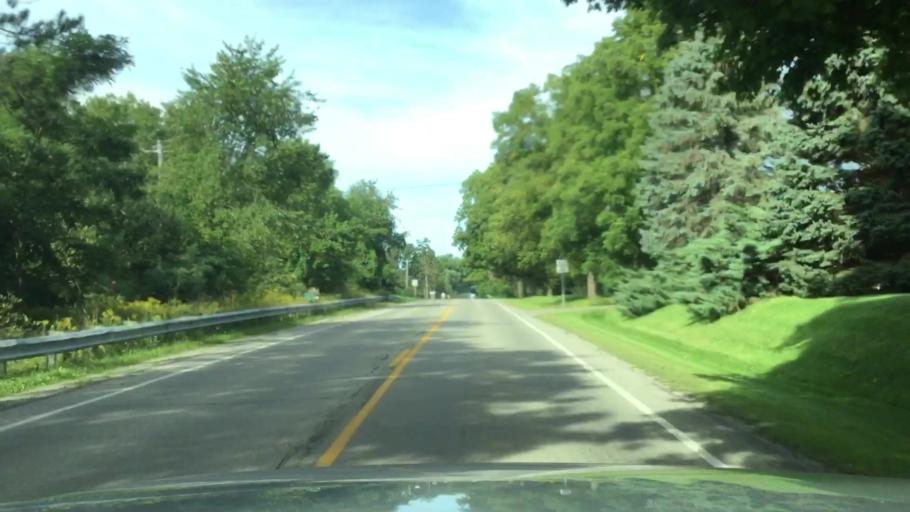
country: US
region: Michigan
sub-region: Genesee County
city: Montrose
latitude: 43.1179
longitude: -83.8949
